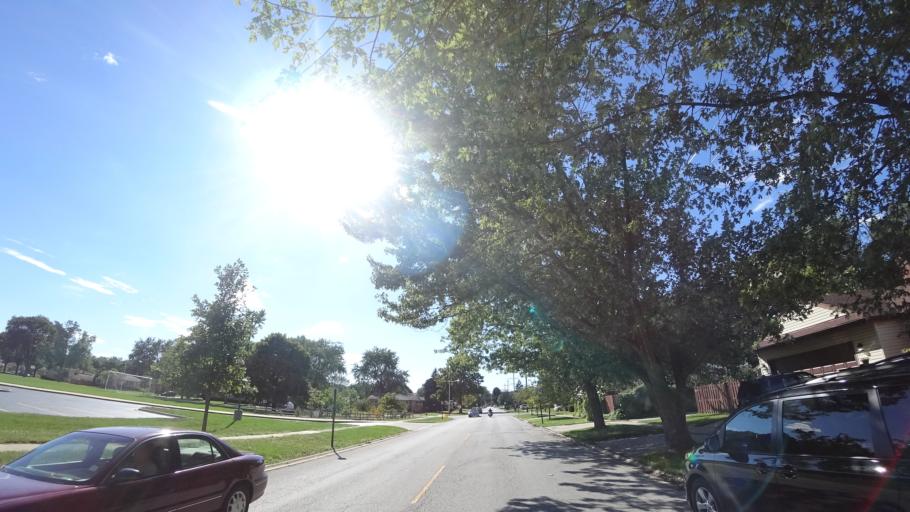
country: US
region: Illinois
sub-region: Cook County
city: Oak Lawn
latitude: 41.7125
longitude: -87.7542
